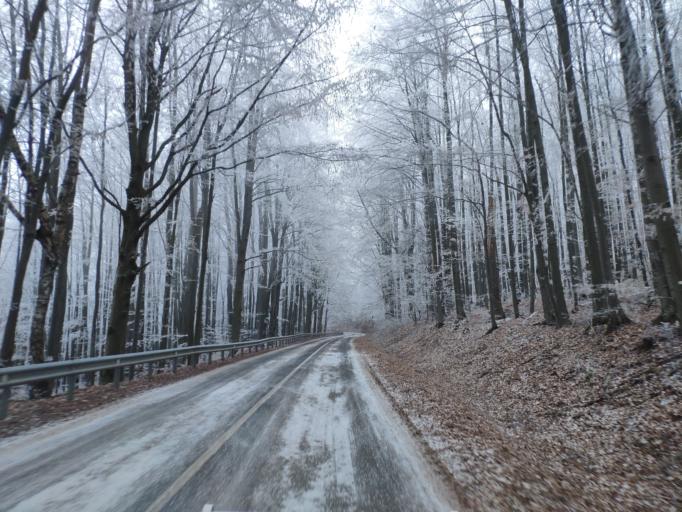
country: SK
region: Kosicky
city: Dobsina
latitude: 48.8028
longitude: 20.4864
